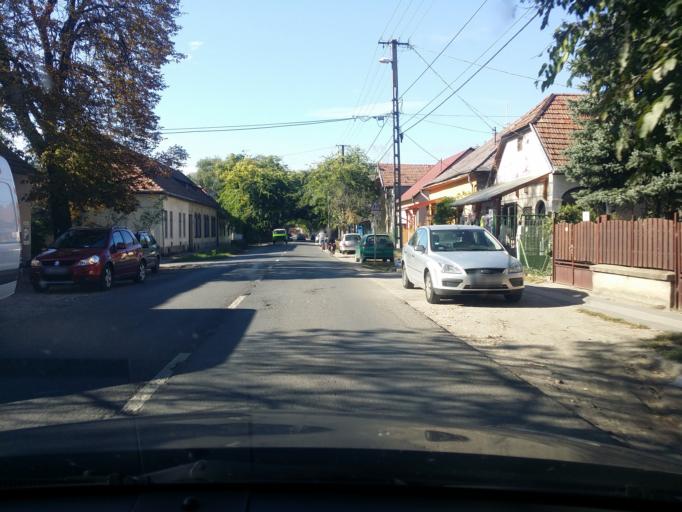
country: HU
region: Pest
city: God
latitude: 47.7034
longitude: 19.1465
